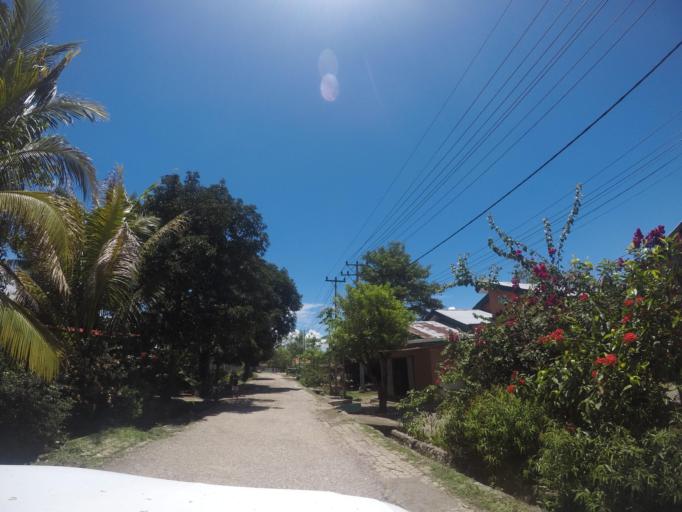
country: TL
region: Bobonaro
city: Maliana
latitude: -8.9892
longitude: 125.2166
